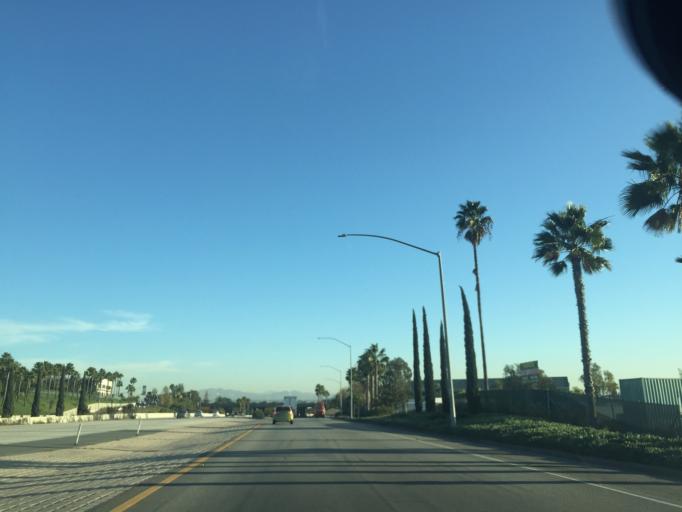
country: MX
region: Baja California
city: Tijuana
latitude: 32.5581
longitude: -116.9427
